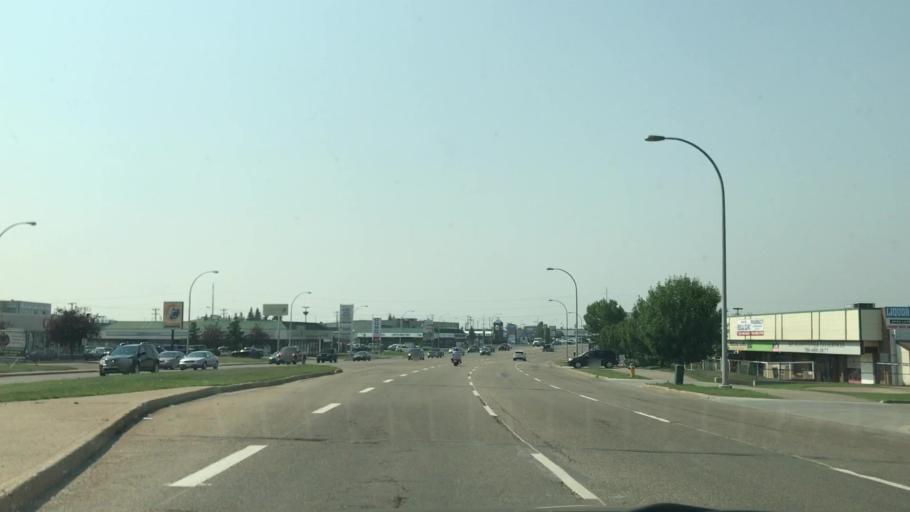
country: CA
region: Alberta
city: Edmonton
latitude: 53.4654
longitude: -113.4707
